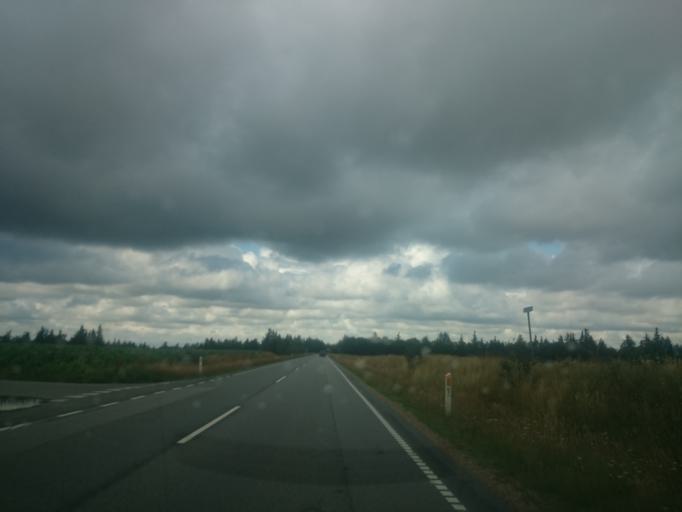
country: DK
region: South Denmark
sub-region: Billund Kommune
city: Grindsted
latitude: 55.6786
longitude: 8.9597
